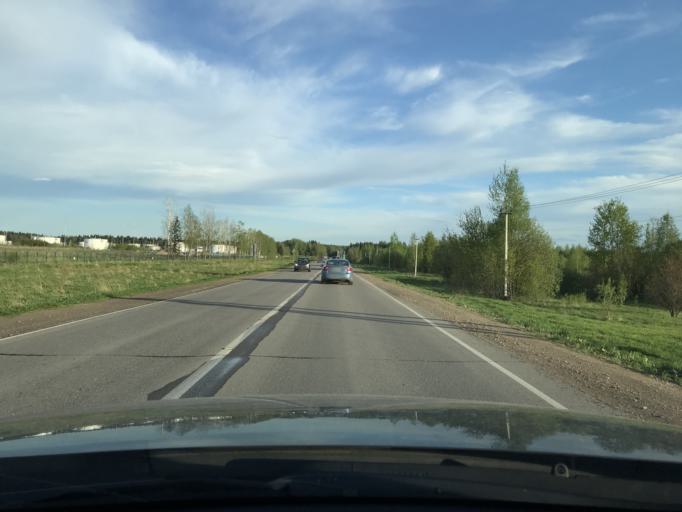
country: RU
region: Moskovskaya
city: Naro-Fominsk
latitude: 55.3719
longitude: 36.6869
